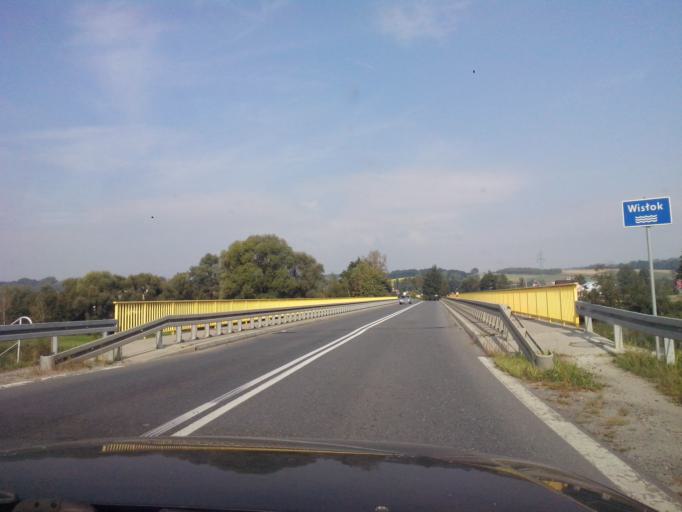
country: PL
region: Subcarpathian Voivodeship
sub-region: Powiat strzyzowski
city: Czudec
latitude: 49.9340
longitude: 21.8172
